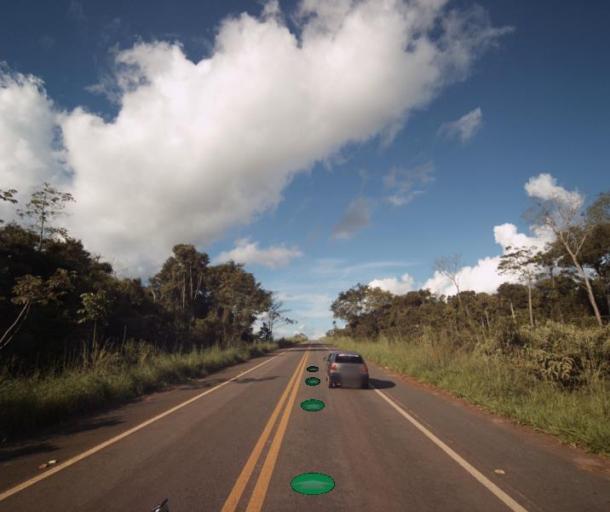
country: BR
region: Goias
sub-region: Itaberai
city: Itaberai
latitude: -15.9968
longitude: -49.7399
